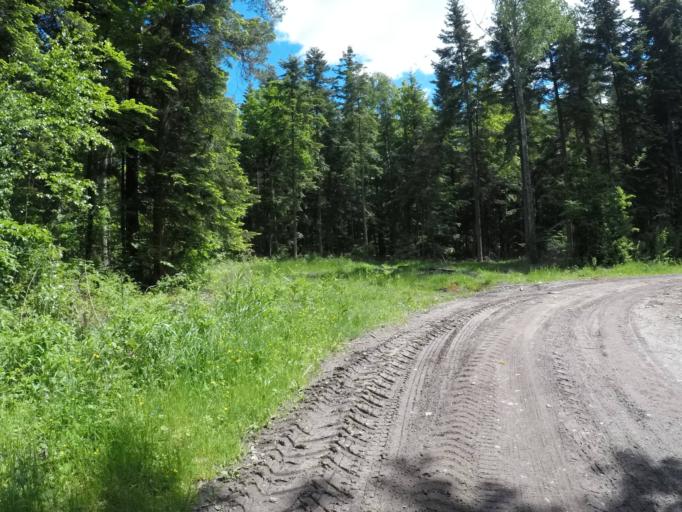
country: PL
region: Swietokrzyskie
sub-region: Powiat kielecki
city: Zagnansk
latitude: 50.9315
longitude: 20.6483
